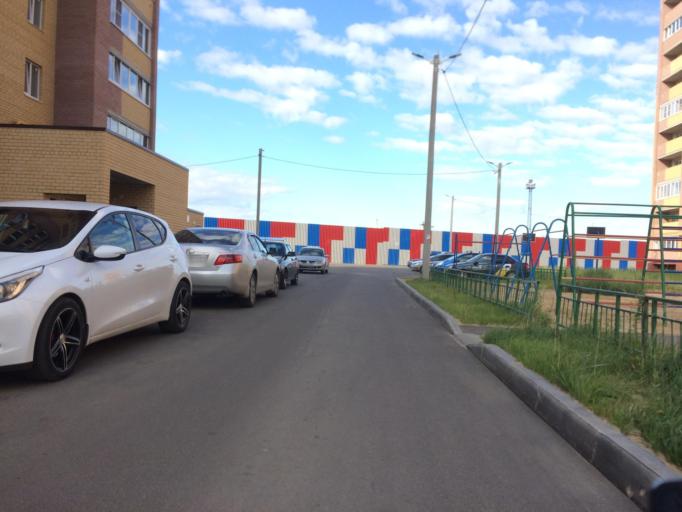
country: RU
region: Mariy-El
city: Yoshkar-Ola
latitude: 56.6252
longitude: 47.8783
